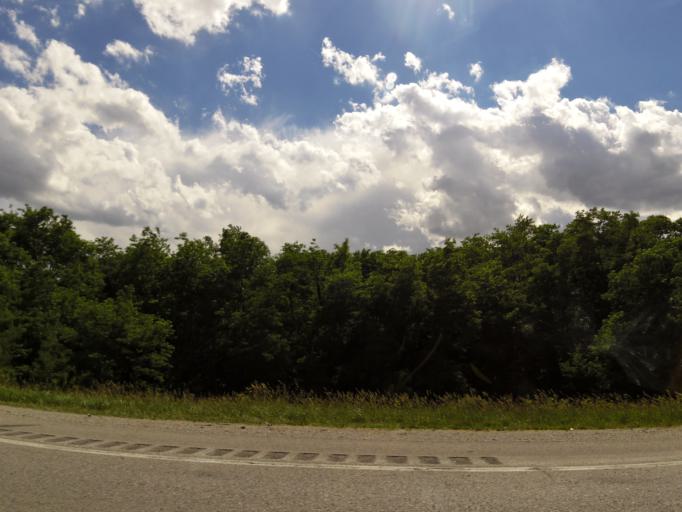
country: US
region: Iowa
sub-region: Johnson County
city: Tiffin
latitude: 41.6788
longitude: -91.6285
